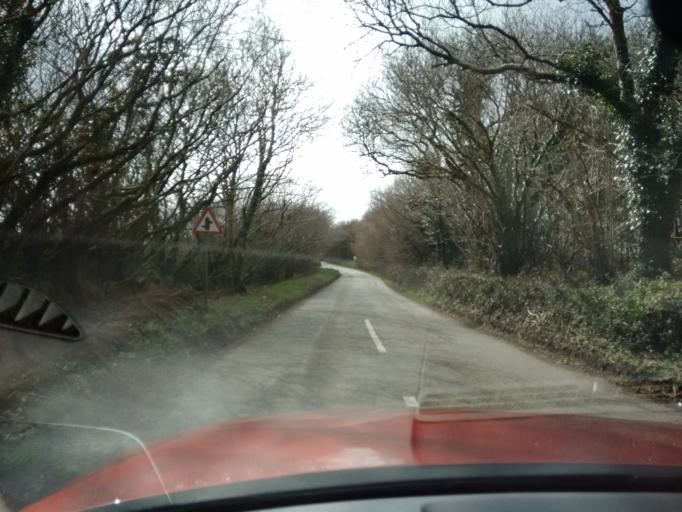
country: GB
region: England
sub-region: Cornwall
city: Liskeard
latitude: 50.4823
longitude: -4.5113
